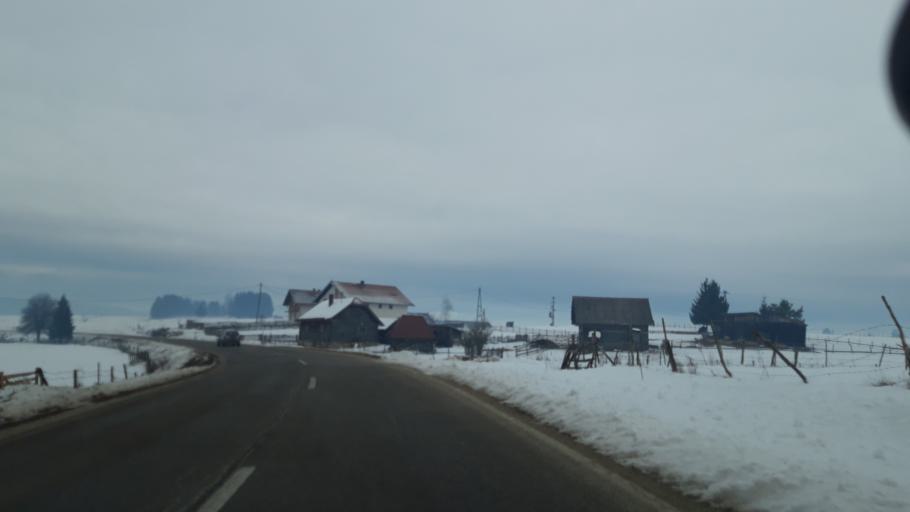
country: BA
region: Republika Srpska
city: Sokolac
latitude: 43.9410
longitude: 18.8283
